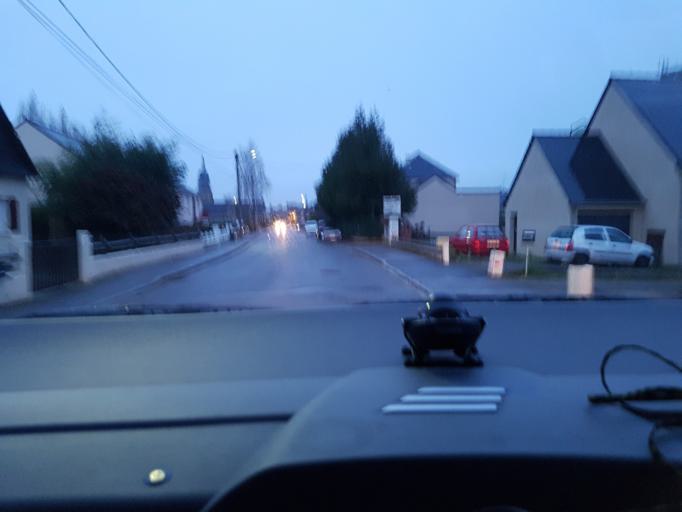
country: FR
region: Brittany
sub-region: Departement d'Ille-et-Vilaine
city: Livre-sur-Changeon
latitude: 48.1799
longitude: -1.3013
